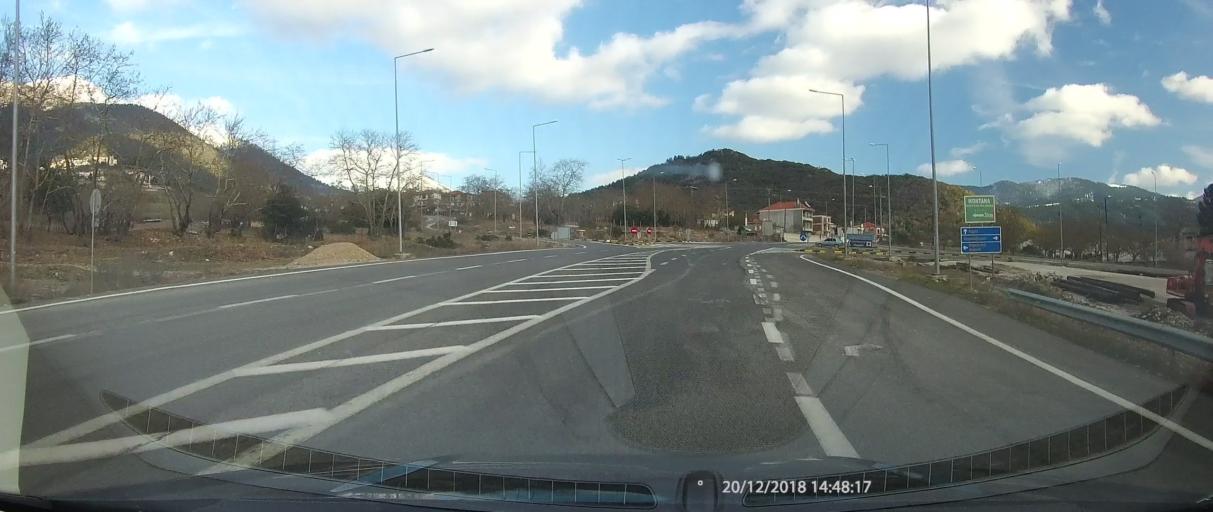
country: GR
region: Central Greece
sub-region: Nomos Evrytanias
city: Karpenisi
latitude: 38.9053
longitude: 21.7878
